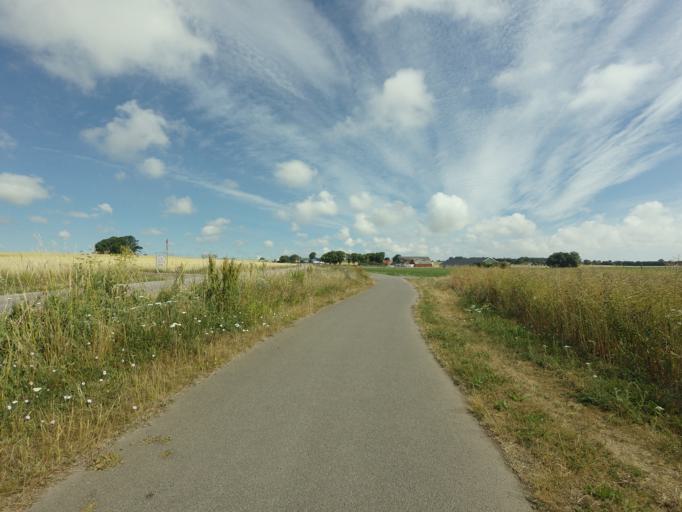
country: SE
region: Skane
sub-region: Simrishamns Kommun
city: Simrishamn
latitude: 55.4806
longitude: 14.2846
